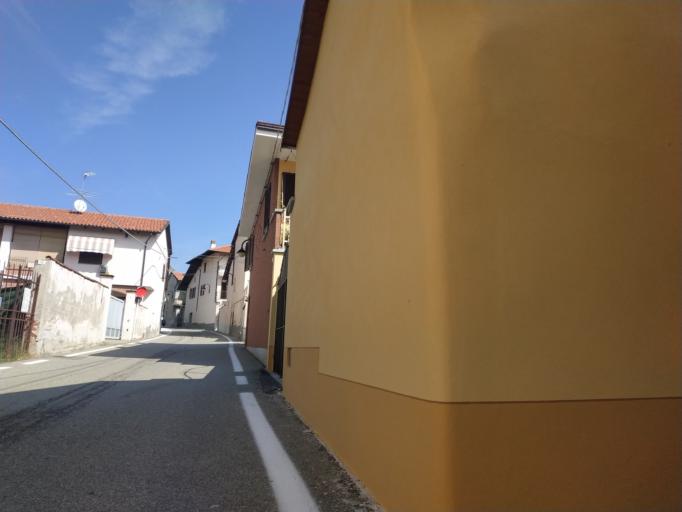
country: IT
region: Piedmont
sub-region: Provincia di Torino
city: Orio Canavese
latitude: 45.3268
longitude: 7.8608
